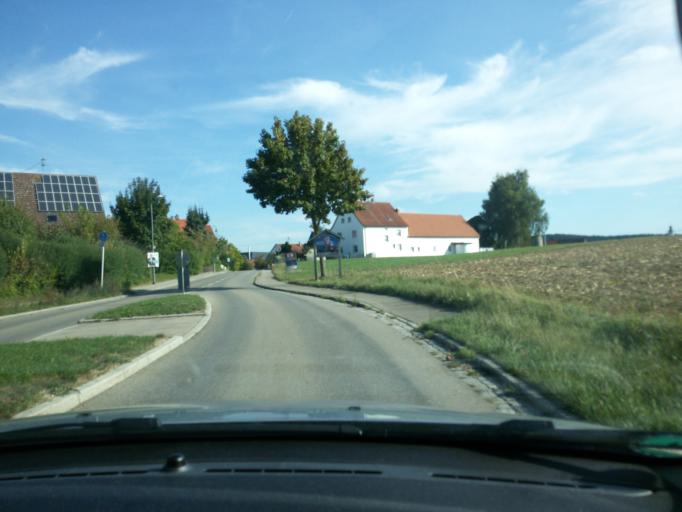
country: DE
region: Bavaria
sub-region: Swabia
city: Kutzenhausen
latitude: 48.3459
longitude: 10.6922
